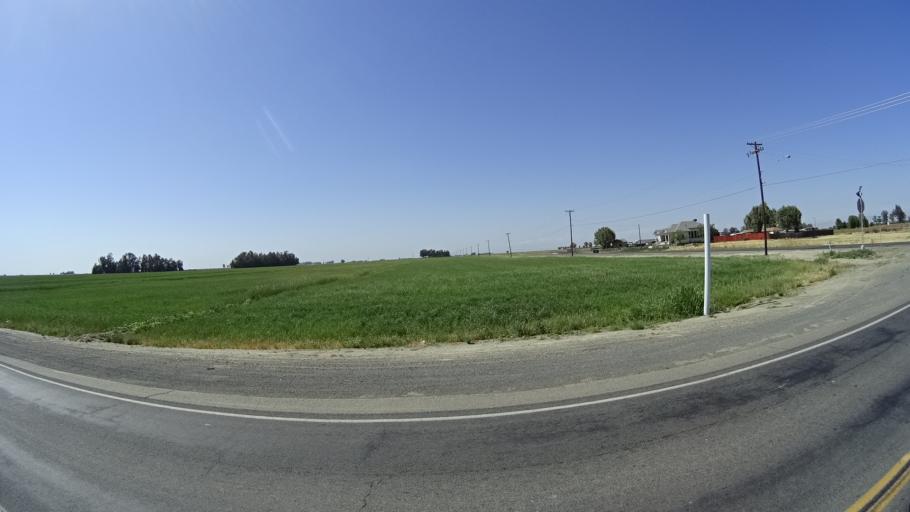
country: US
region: California
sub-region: Kings County
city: Stratford
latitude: 36.2113
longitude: -119.7797
